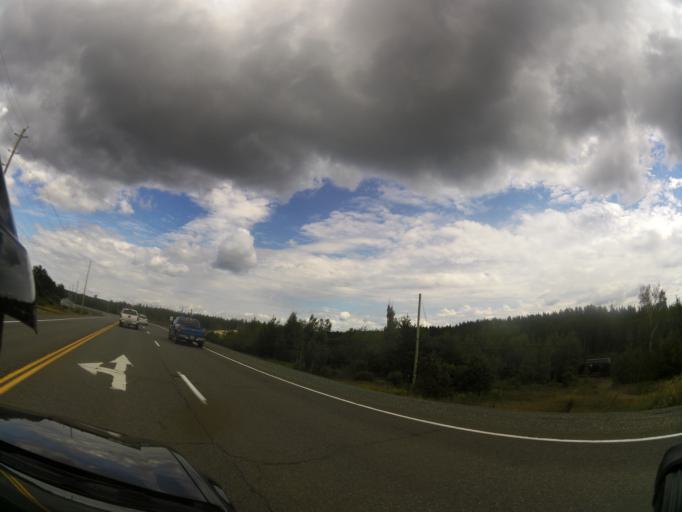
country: CA
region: Ontario
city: Greater Sudbury
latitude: 46.5120
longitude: -80.7008
